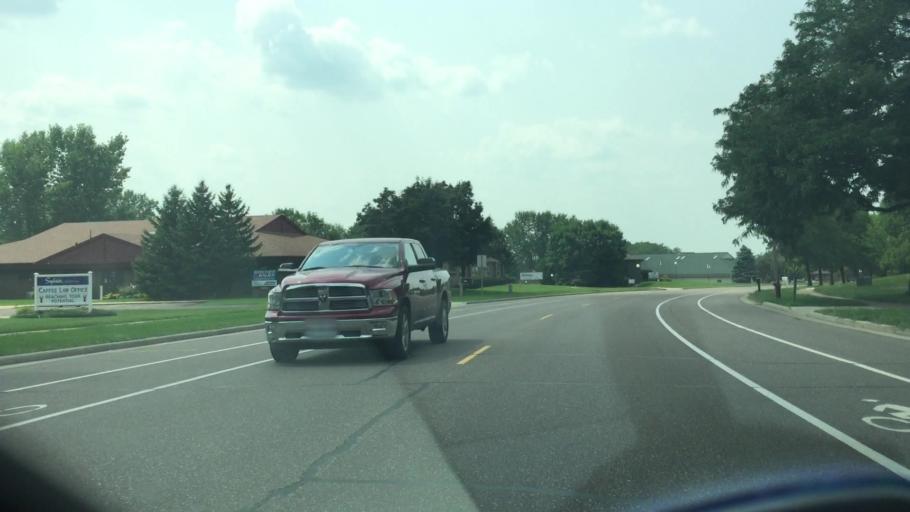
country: US
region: Wisconsin
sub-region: Eau Claire County
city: Altoona
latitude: 44.7687
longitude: -91.4533
